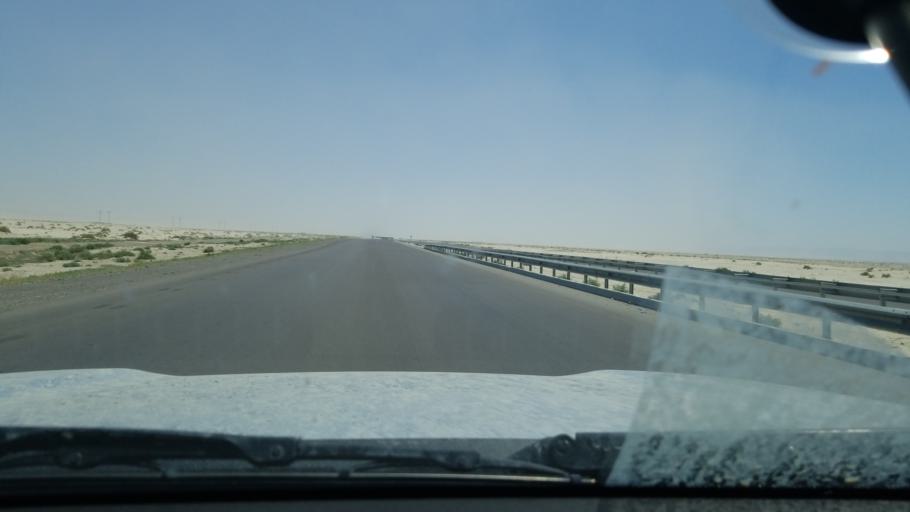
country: TM
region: Balkan
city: Gumdag
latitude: 39.1933
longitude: 54.9909
